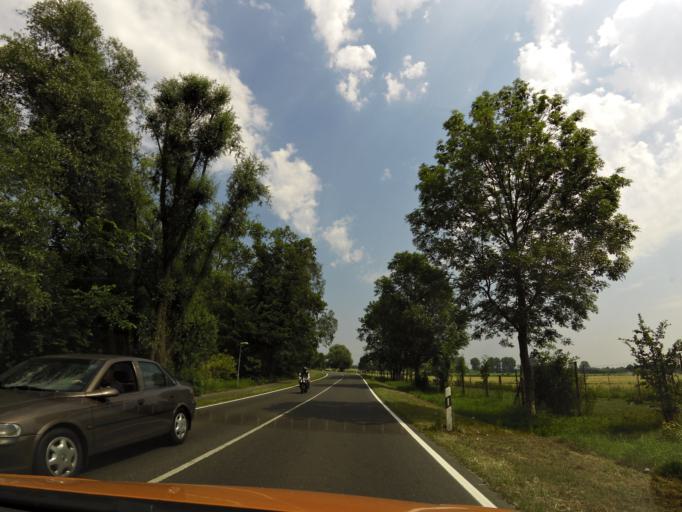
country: DE
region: Brandenburg
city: Wustermark
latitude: 52.5379
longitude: 12.9302
